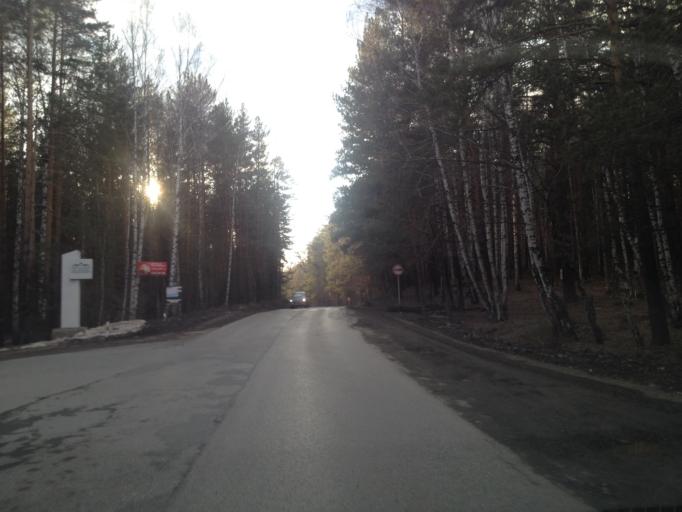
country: RU
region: Sverdlovsk
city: Shirokaya Rechka
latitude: 56.8148
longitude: 60.4358
